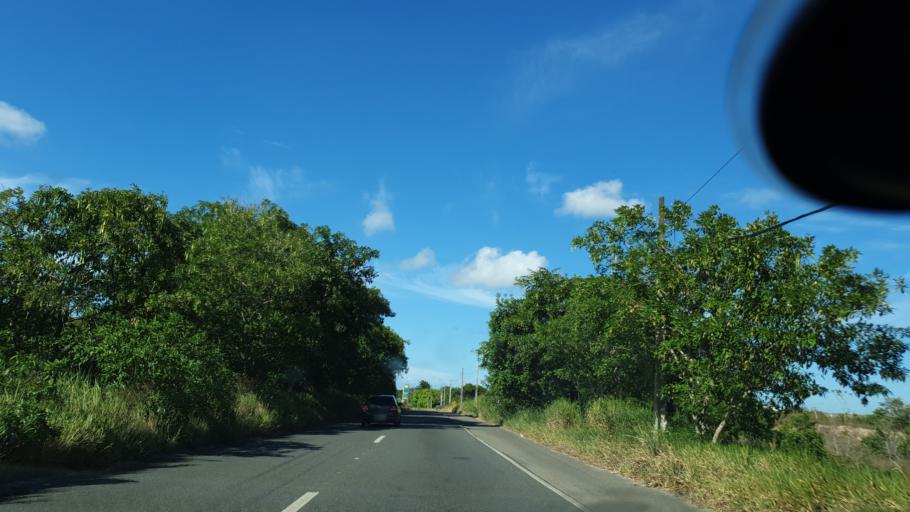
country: BR
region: Bahia
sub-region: Camacari
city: Camacari
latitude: -12.6779
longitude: -38.3016
